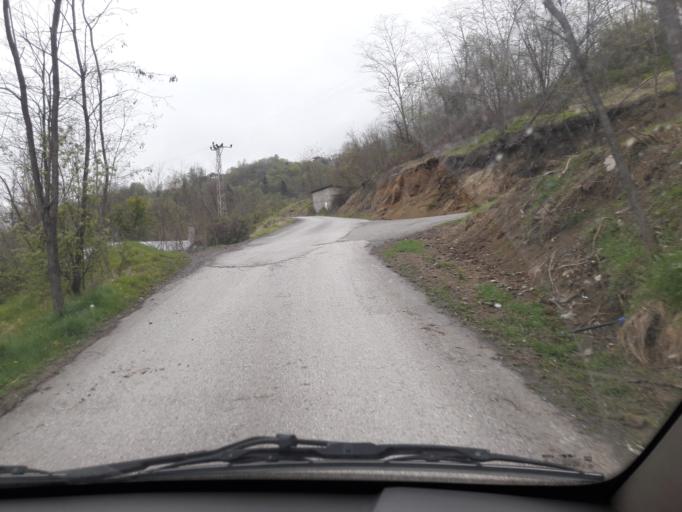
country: TR
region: Trabzon
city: Duzkoy
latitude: 40.9305
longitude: 39.4789
